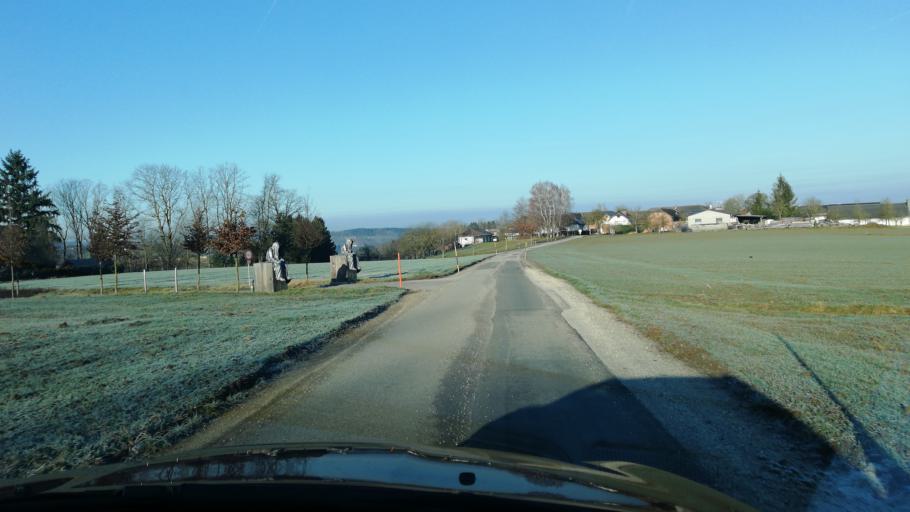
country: AT
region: Upper Austria
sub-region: Politischer Bezirk Steyr-Land
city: Bad Hall
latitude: 48.0416
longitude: 14.2246
